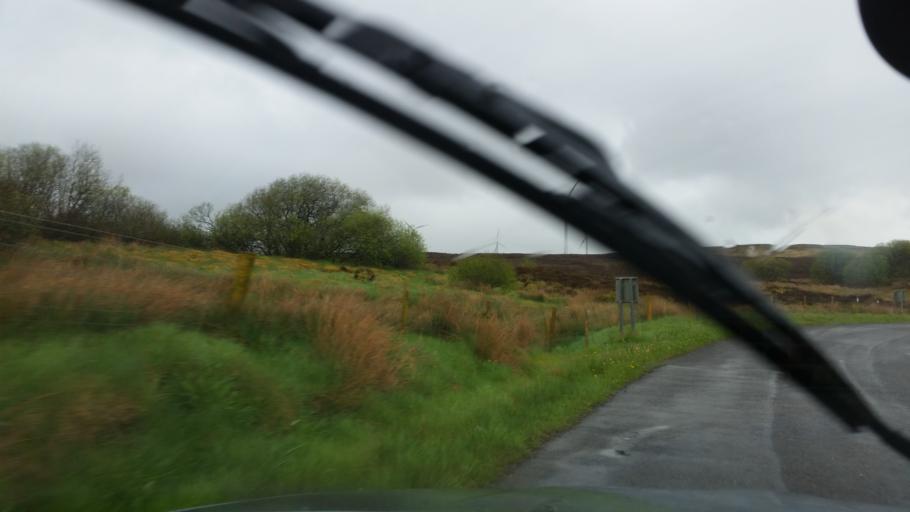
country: GB
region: Northern Ireland
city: Fivemiletown
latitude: 54.4305
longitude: -7.3315
